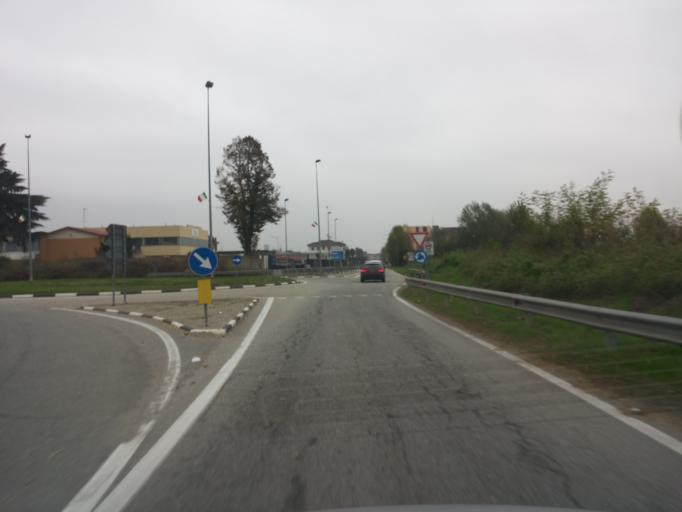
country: IT
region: Piedmont
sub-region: Provincia di Vercelli
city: Borgo Vercelli
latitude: 45.3517
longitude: 8.4592
